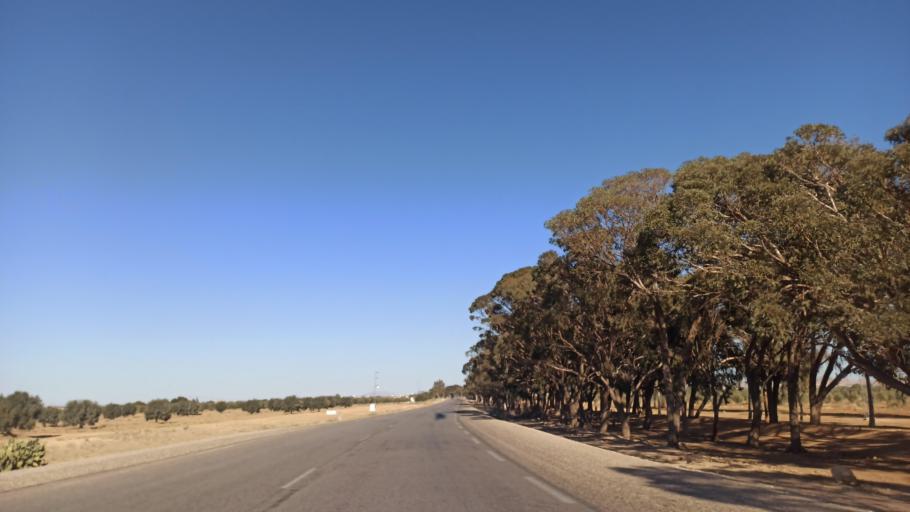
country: TN
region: Sidi Bu Zayd
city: Jilma
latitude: 35.2413
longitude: 9.3910
